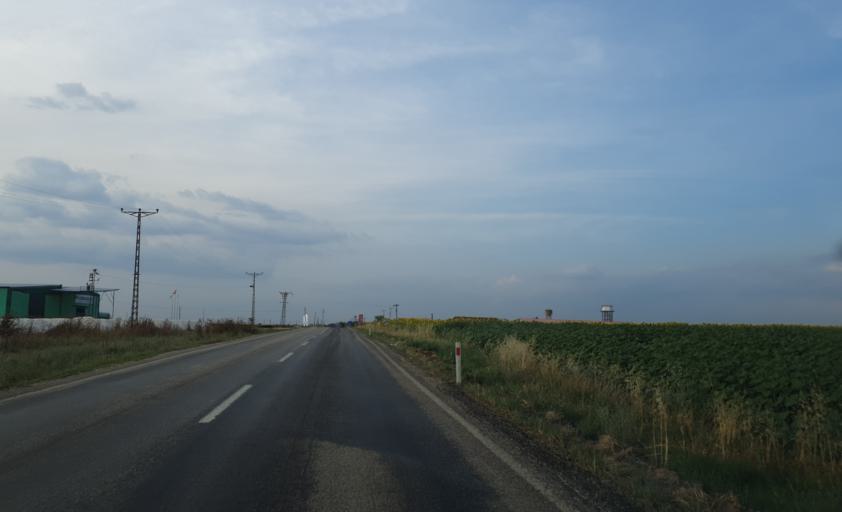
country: TR
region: Kirklareli
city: Babaeski
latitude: 41.3424
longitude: 27.1409
